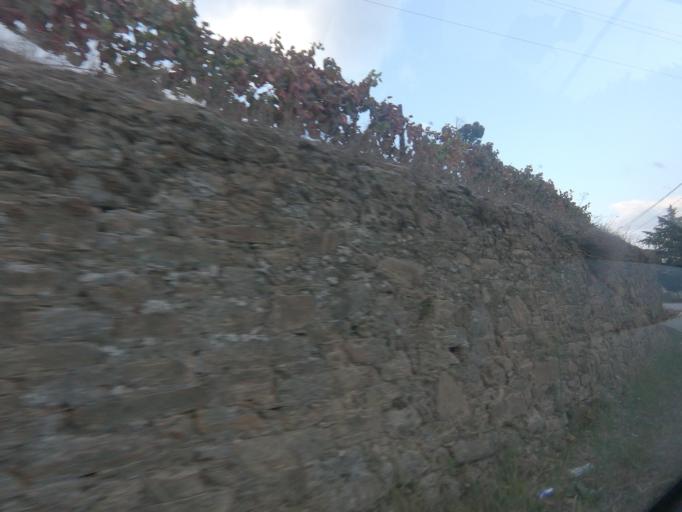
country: PT
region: Vila Real
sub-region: Mesao Frio
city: Mesao Frio
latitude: 41.1788
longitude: -7.8604
